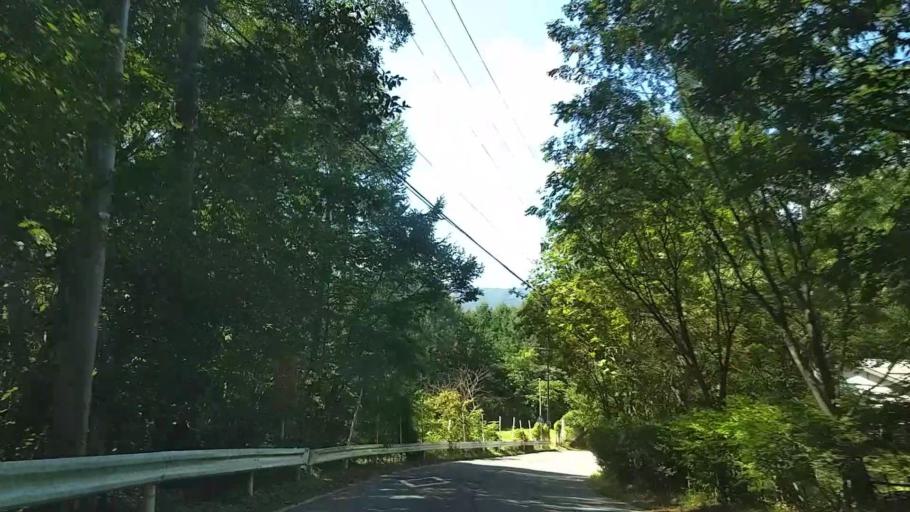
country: JP
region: Nagano
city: Matsumoto
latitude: 36.2106
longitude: 138.0984
